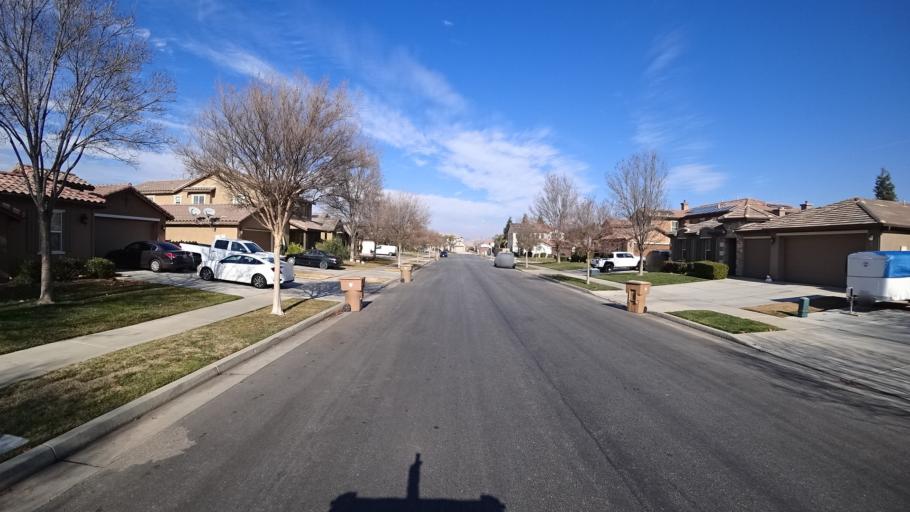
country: US
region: California
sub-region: Kern County
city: Oildale
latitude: 35.4048
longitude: -118.8957
